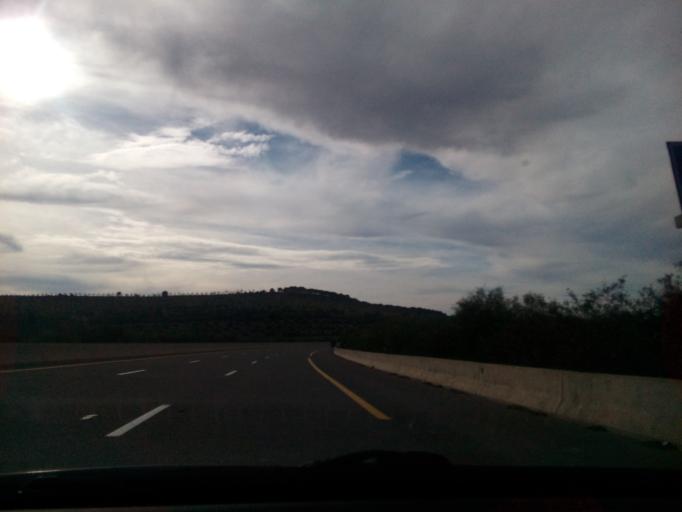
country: DZ
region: Sidi Bel Abbes
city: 'Ain el Berd
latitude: 35.3718
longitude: -0.4997
